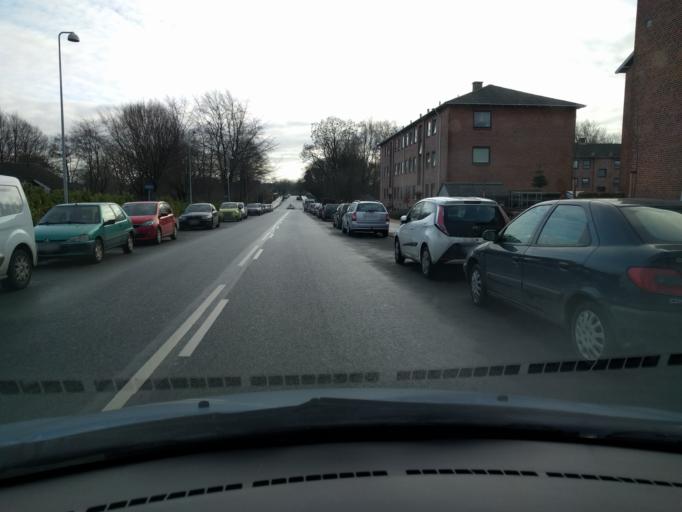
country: DK
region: South Denmark
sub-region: Odense Kommune
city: Odense
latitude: 55.3906
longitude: 10.4110
